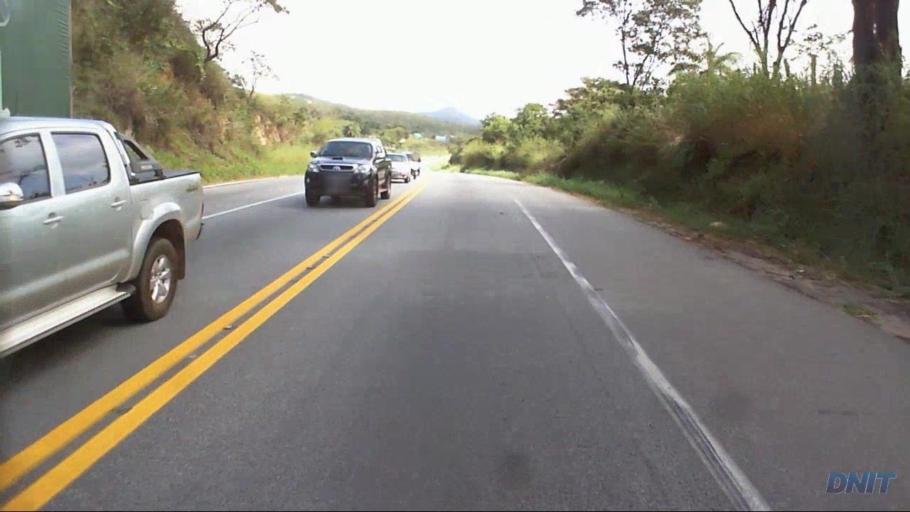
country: BR
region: Minas Gerais
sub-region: Santa Luzia
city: Santa Luzia
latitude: -19.8106
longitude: -43.7947
